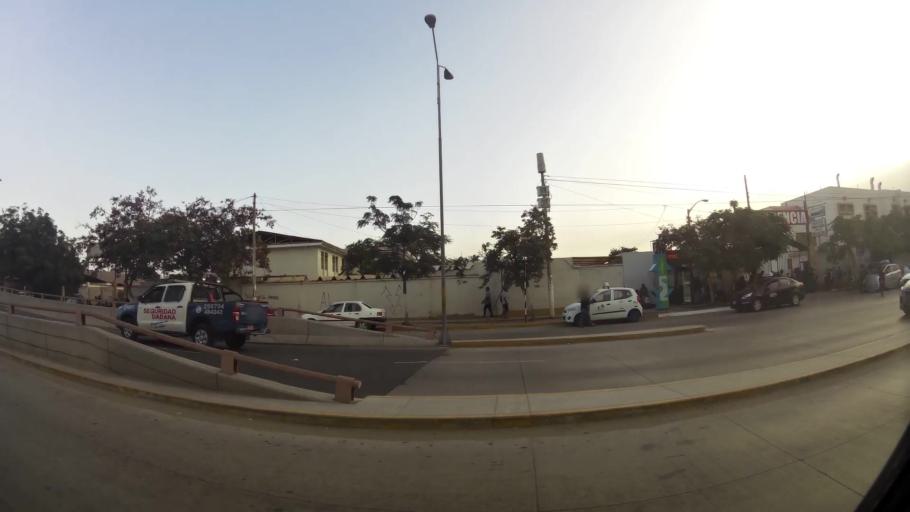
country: PE
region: La Libertad
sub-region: Provincia de Trujillo
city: Trujillo
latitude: -8.1043
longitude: -79.0365
